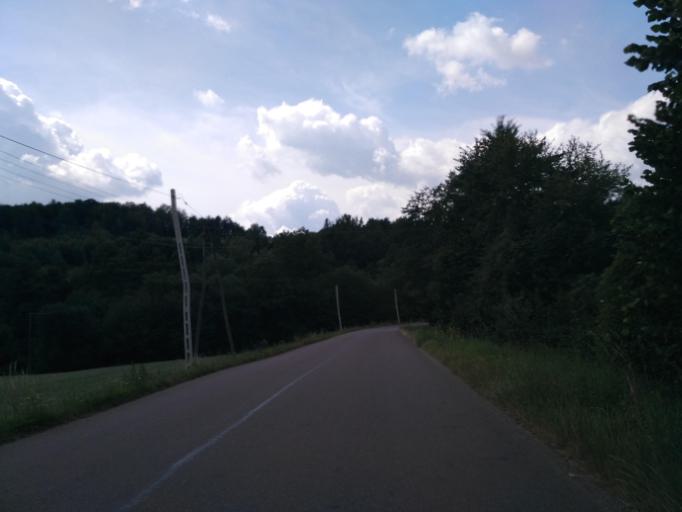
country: PL
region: Subcarpathian Voivodeship
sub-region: Powiat debicki
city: Brzostek
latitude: 49.9160
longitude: 21.3701
